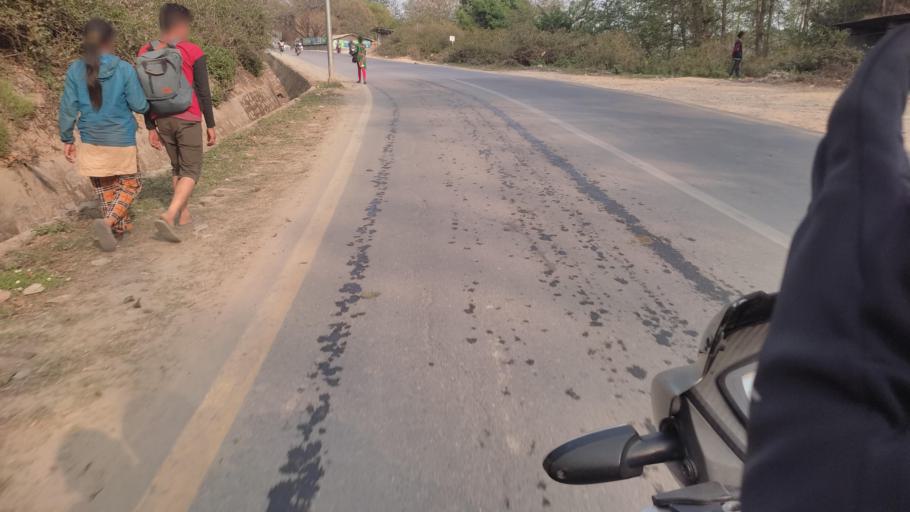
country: NP
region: Central Region
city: Kirtipur
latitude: 27.6607
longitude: 85.2910
